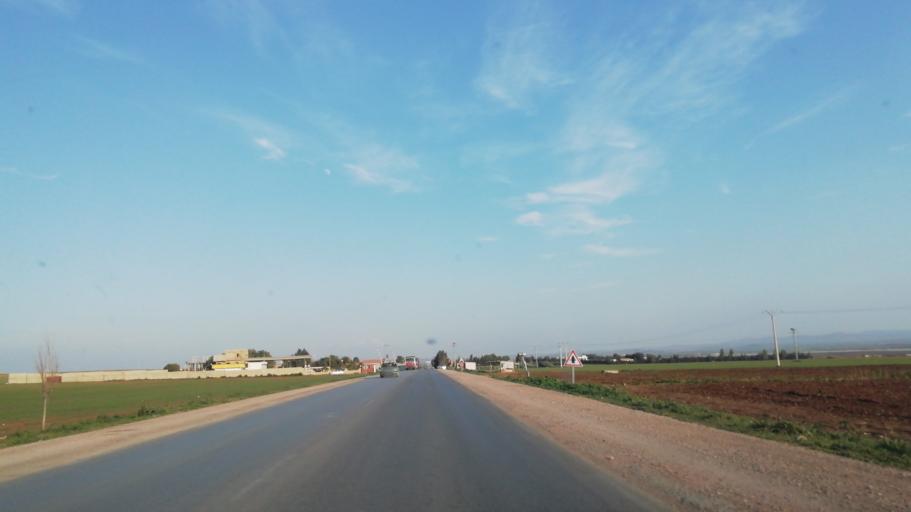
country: DZ
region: Relizane
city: Djidiouia
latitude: 35.8945
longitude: 0.6571
